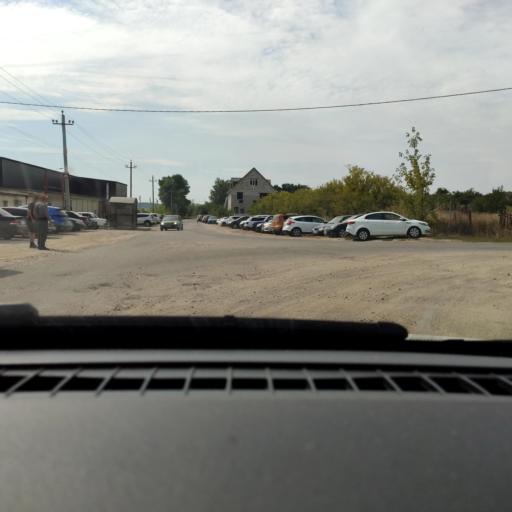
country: RU
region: Voronezj
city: Pridonskoy
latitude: 51.7349
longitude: 39.0619
